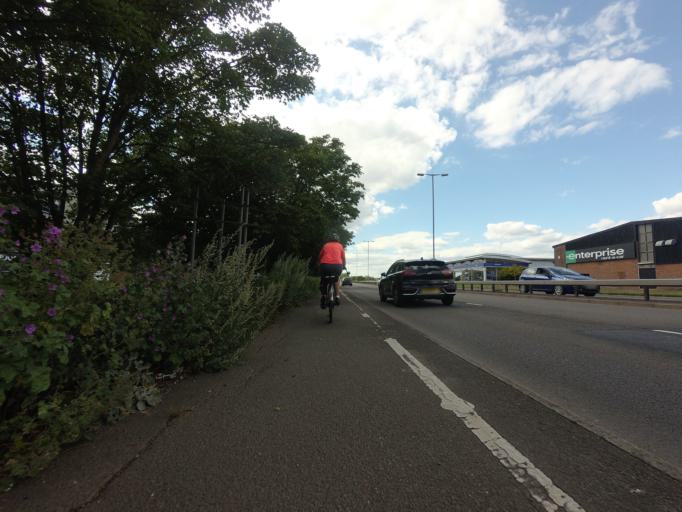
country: GB
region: England
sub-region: East Sussex
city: Eastbourne
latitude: 50.7899
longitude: 0.2980
